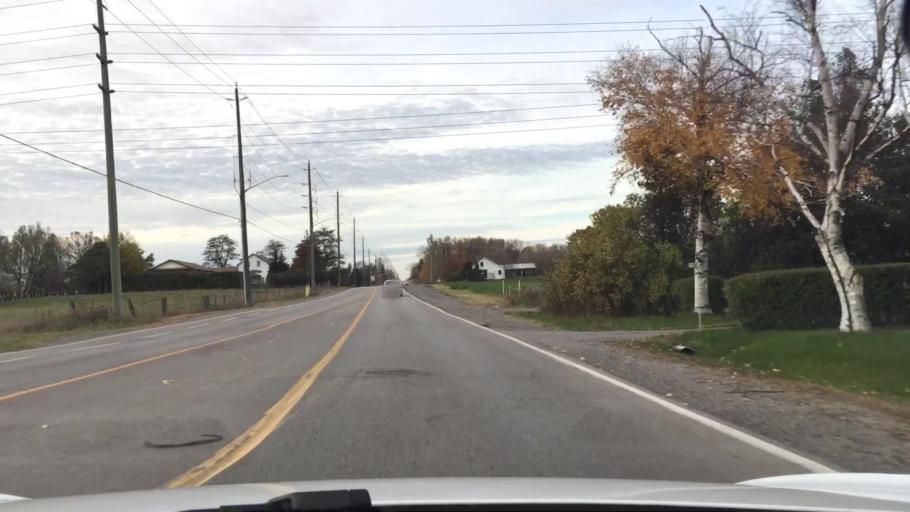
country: CA
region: Ontario
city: Oshawa
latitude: 43.9314
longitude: -78.8242
